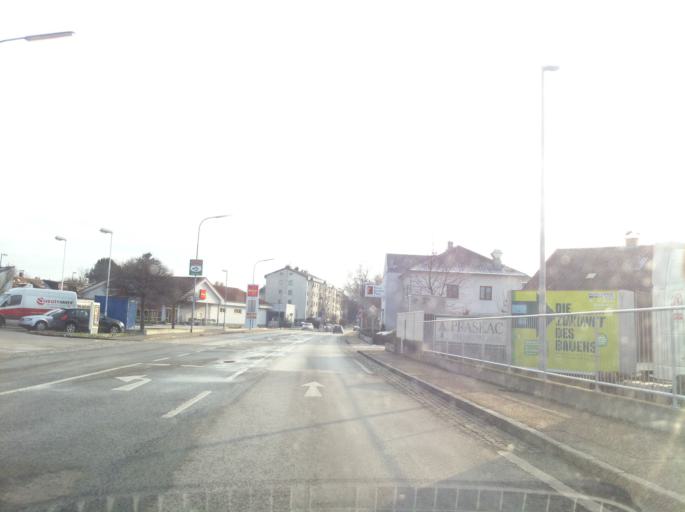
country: AT
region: Lower Austria
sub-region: Politischer Bezirk Tulln
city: Tulln
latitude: 48.3267
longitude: 16.0587
